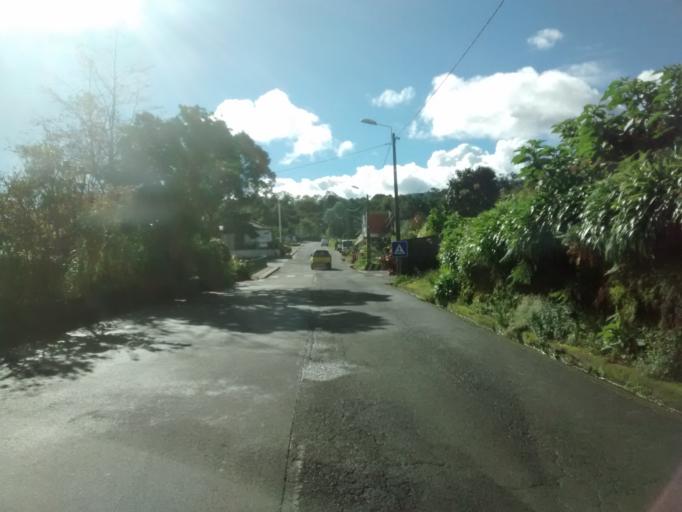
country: PT
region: Madeira
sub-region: Santana
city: Santana
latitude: 32.8043
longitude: -16.8816
